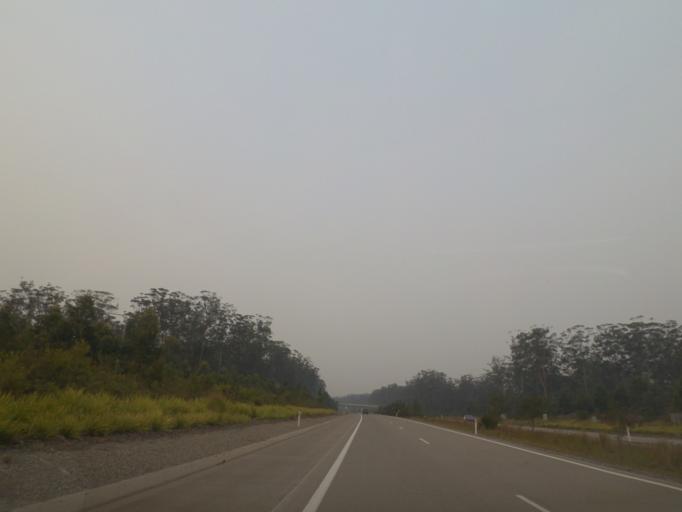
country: AU
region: New South Wales
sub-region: Kempsey
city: Frederickton
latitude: -30.9087
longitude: 152.9188
